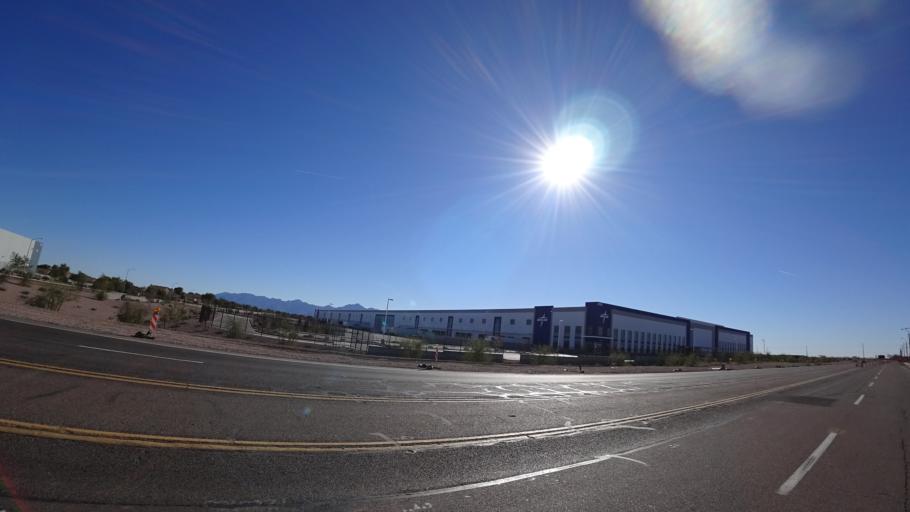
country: US
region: Arizona
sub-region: Maricopa County
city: Tolleson
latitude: 33.4365
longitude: -112.2472
